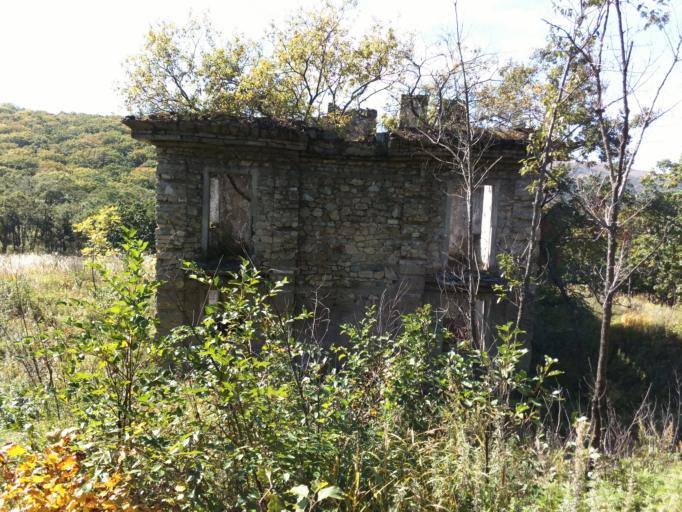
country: RU
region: Primorskiy
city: Zarubino
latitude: 42.6957
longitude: 131.2368
